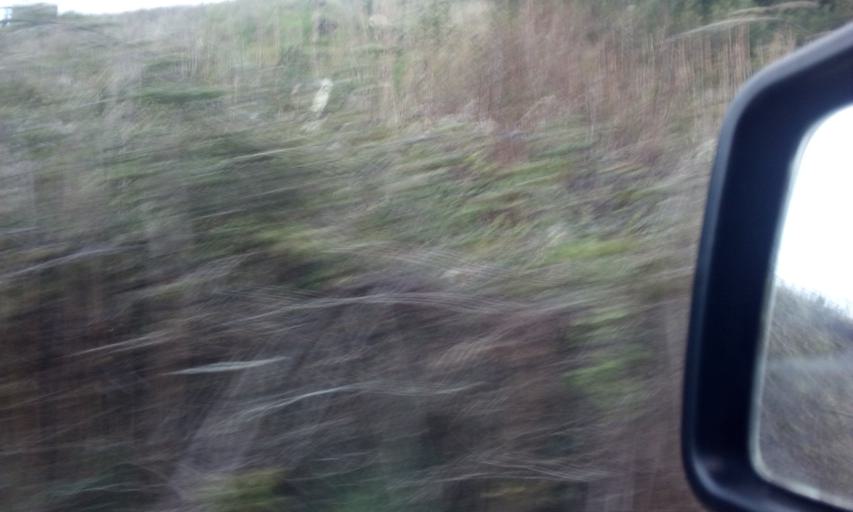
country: PT
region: Guarda
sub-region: Celorico da Beira
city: Celorico da Beira
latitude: 40.6313
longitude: -7.4325
